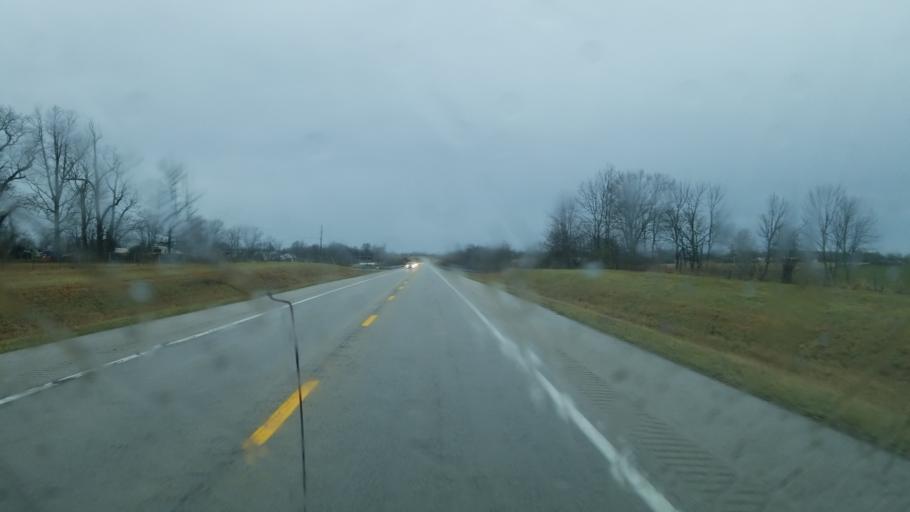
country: US
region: Ohio
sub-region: Adams County
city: Manchester
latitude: 38.5608
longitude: -83.6074
